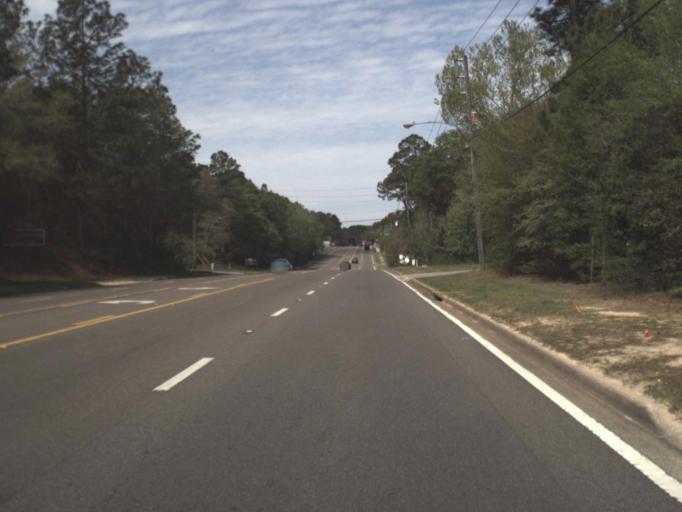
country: US
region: Florida
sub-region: Okaloosa County
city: Crestview
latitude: 30.7613
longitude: -86.5554
